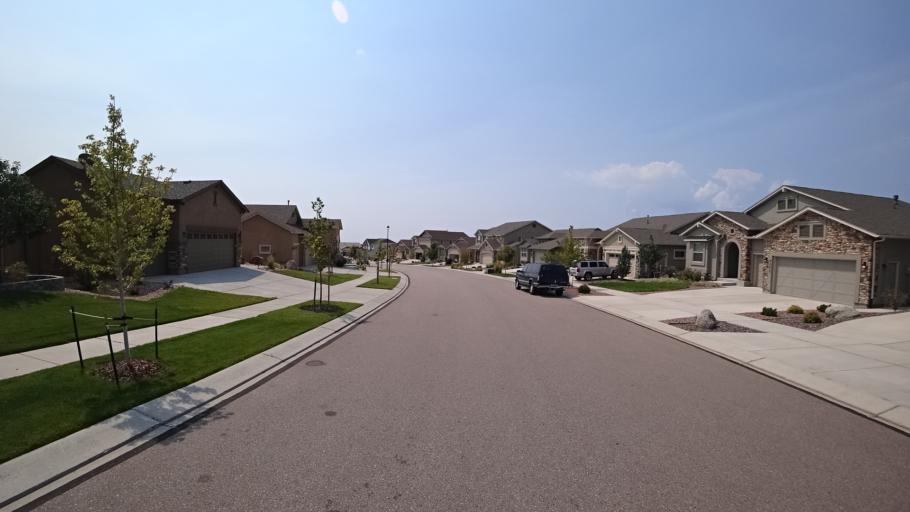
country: US
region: Colorado
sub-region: El Paso County
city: Black Forest
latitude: 38.9637
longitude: -104.7267
